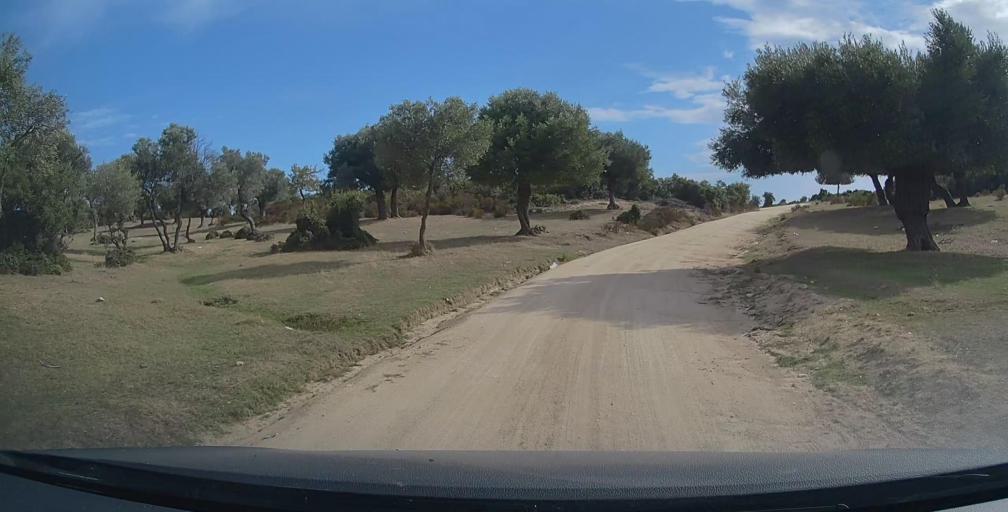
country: GR
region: Central Macedonia
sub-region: Nomos Chalkidikis
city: Sykia
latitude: 40.0032
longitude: 23.9245
